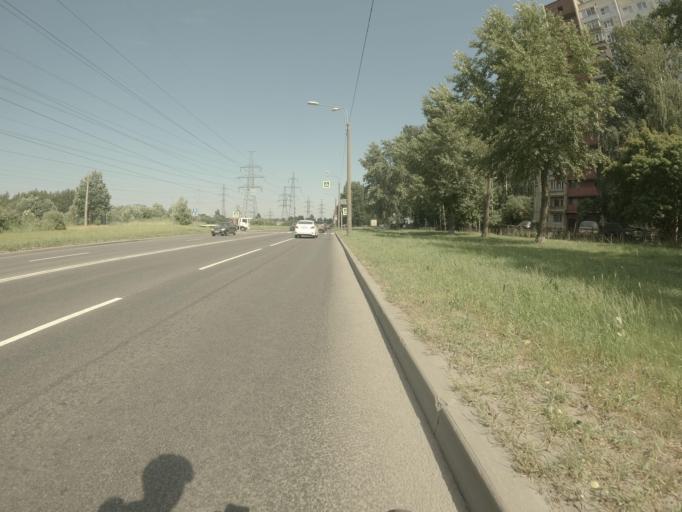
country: RU
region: St.-Petersburg
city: Krasnogvargeisky
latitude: 59.9499
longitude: 30.4609
